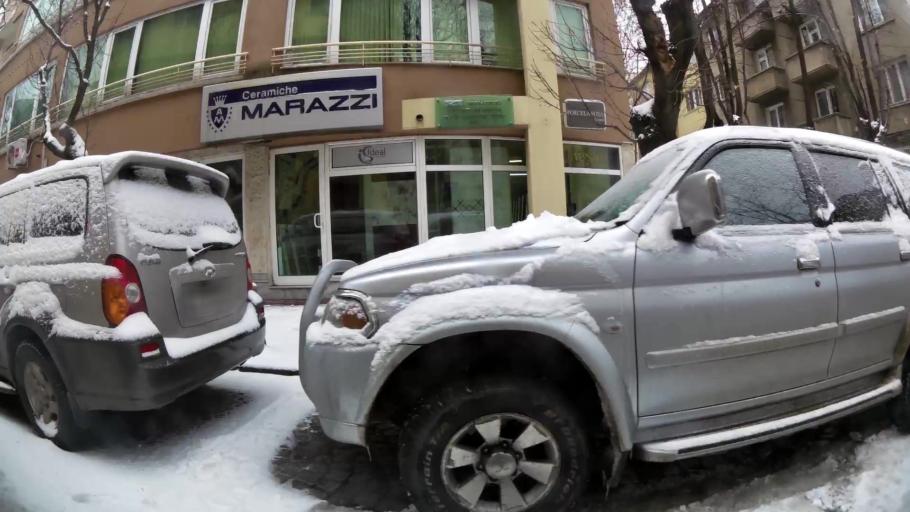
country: BG
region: Sofia-Capital
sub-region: Stolichna Obshtina
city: Sofia
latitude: 42.6893
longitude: 23.3117
